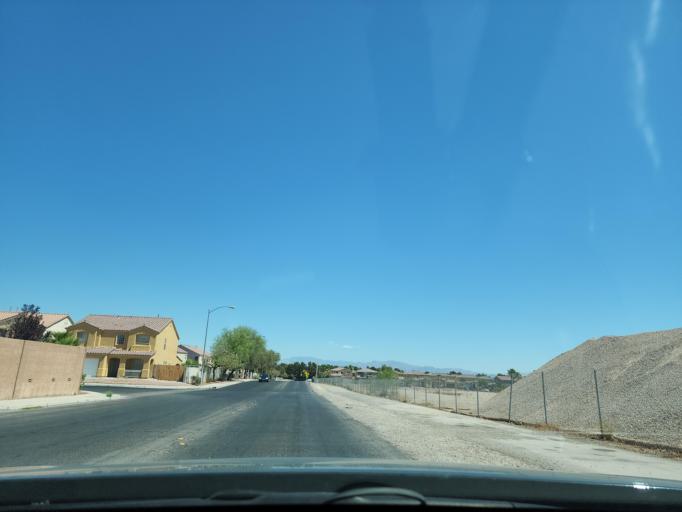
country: US
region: Nevada
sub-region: Clark County
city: Spring Valley
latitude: 36.0883
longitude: -115.2520
